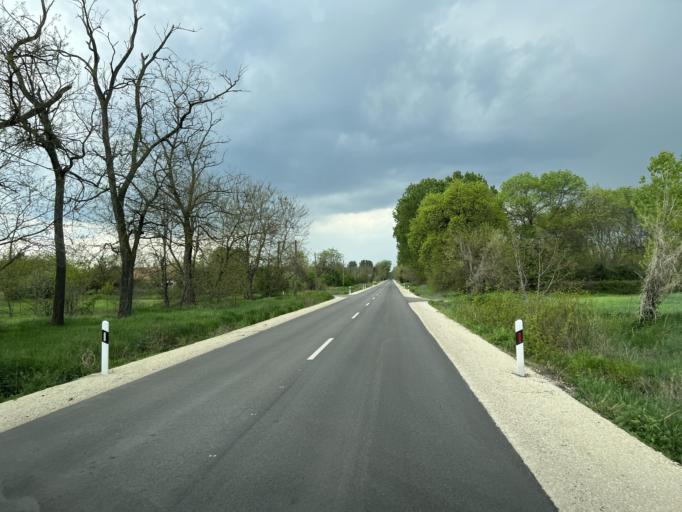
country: HU
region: Pest
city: Nagykoros
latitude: 47.0423
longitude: 19.7432
